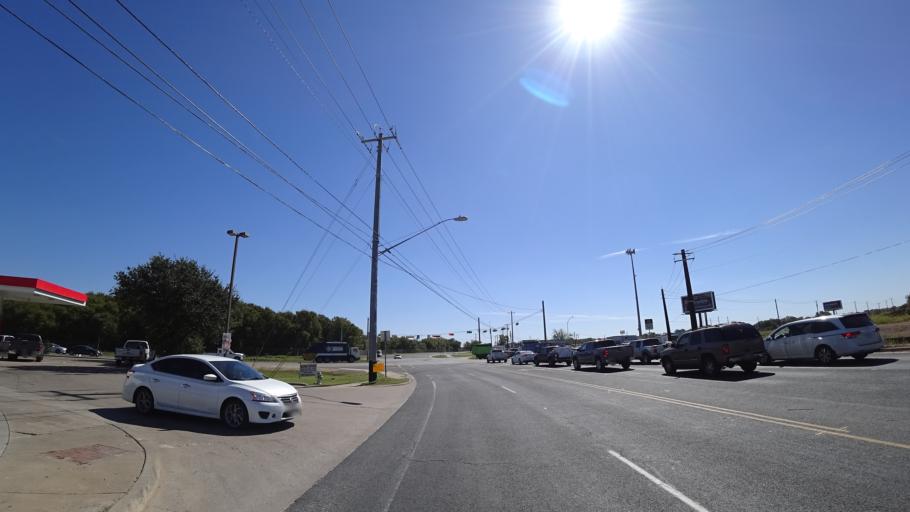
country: US
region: Texas
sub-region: Travis County
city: Austin
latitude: 30.1833
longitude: -97.6883
